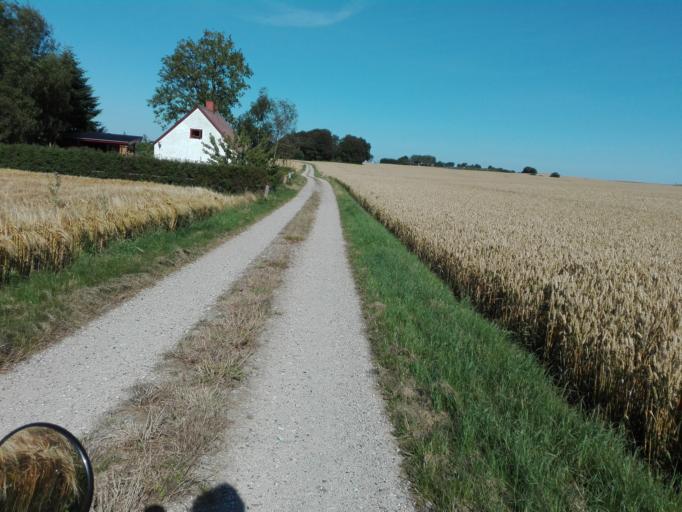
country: DK
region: Central Jutland
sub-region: Odder Kommune
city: Odder
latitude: 55.9522
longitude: 10.0958
